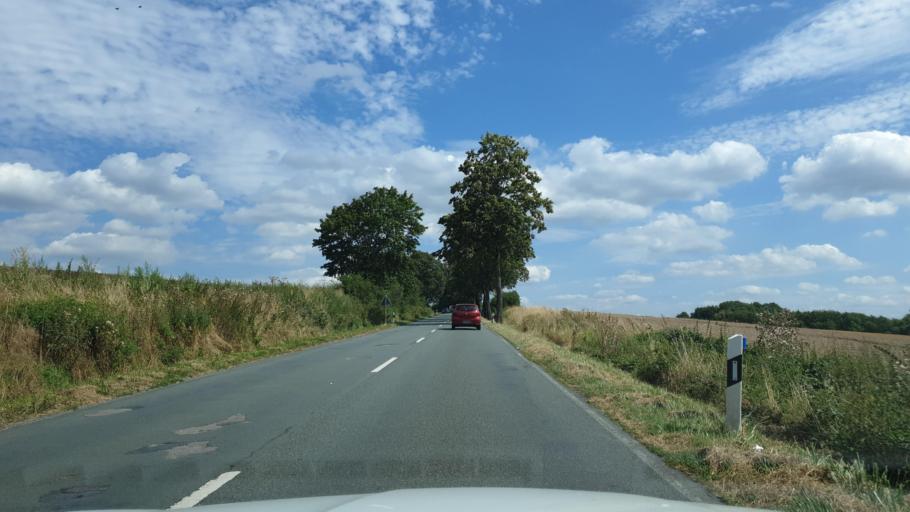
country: DE
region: North Rhine-Westphalia
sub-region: Regierungsbezirk Detmold
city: Herford
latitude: 52.1146
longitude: 8.6318
